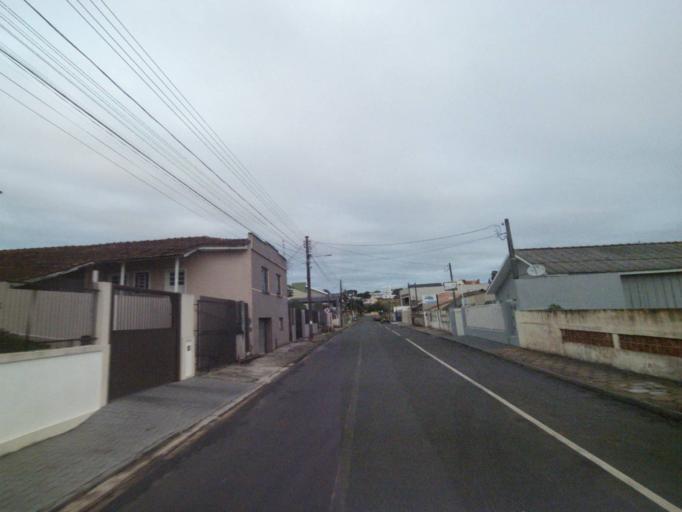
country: BR
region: Parana
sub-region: Telemaco Borba
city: Telemaco Borba
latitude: -24.3240
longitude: -50.6191
